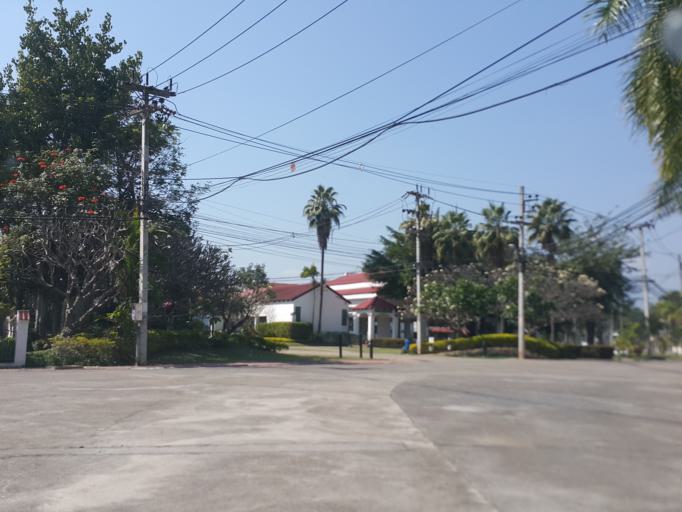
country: TH
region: Chiang Mai
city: Saraphi
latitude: 18.7597
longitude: 99.0234
